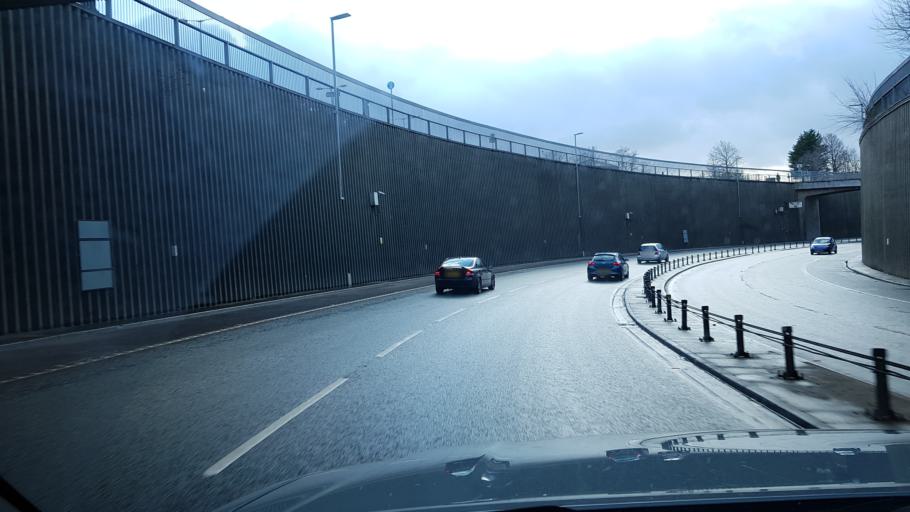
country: GB
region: England
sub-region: Liverpool
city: Liverpool
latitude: 53.4177
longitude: -2.9782
